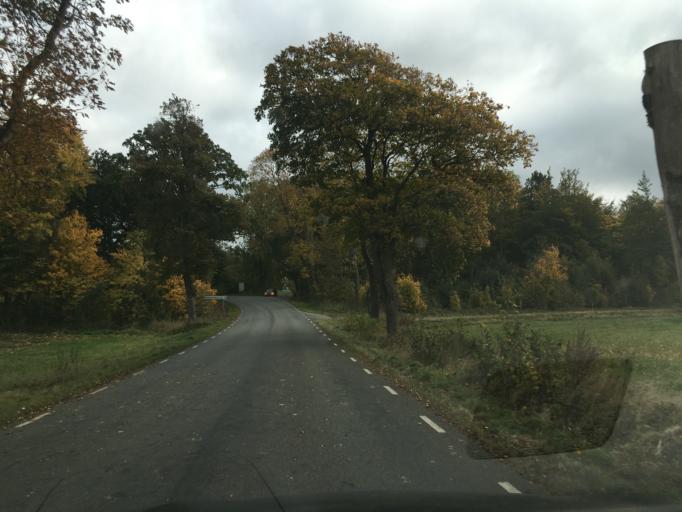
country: SE
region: Skane
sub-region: Tomelilla Kommun
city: Tomelilla
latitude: 55.6448
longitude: 14.0426
